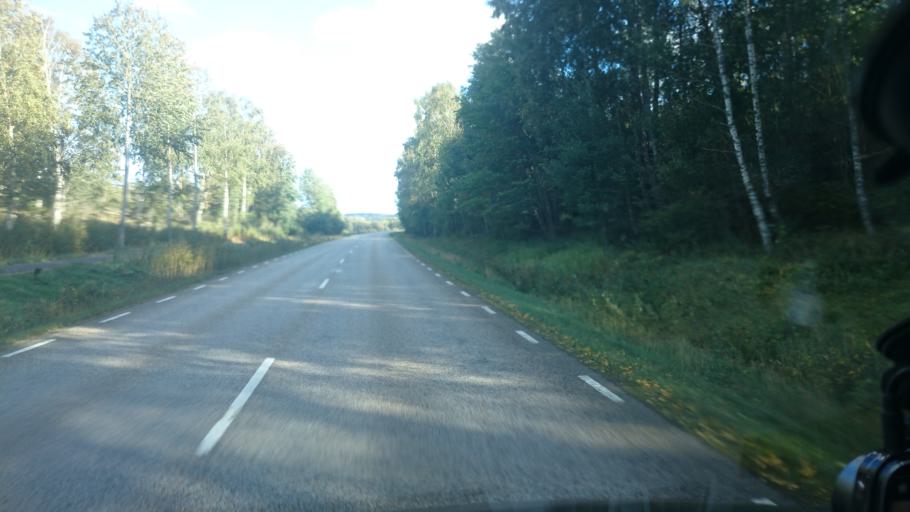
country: SE
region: Vaestra Goetaland
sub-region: Lysekils Kommun
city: Lysekil
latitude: 58.3338
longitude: 11.4425
